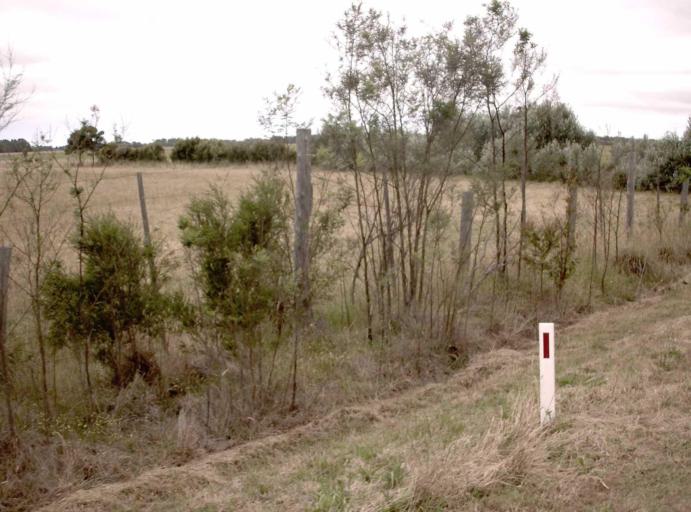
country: AU
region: Victoria
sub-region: Latrobe
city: Traralgon
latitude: -38.4805
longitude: 146.8211
